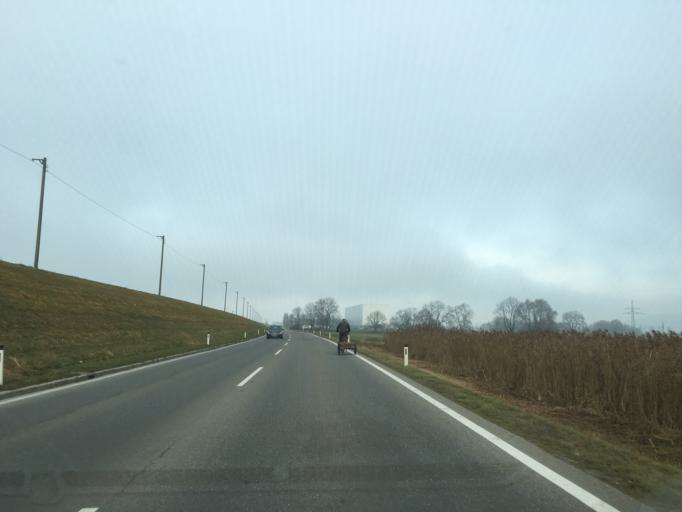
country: AT
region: Vorarlberg
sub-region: Politischer Bezirk Bregenz
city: Fussach
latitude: 47.4602
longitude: 9.6703
